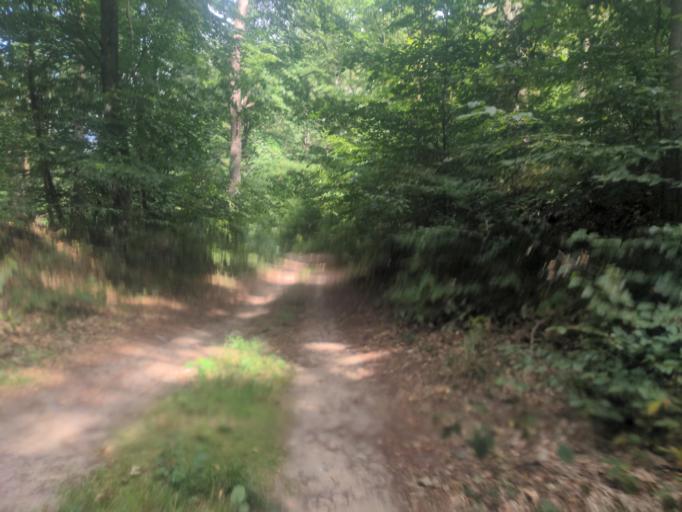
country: DE
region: Lower Saxony
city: Neu Darchau
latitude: 53.2226
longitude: 10.8586
